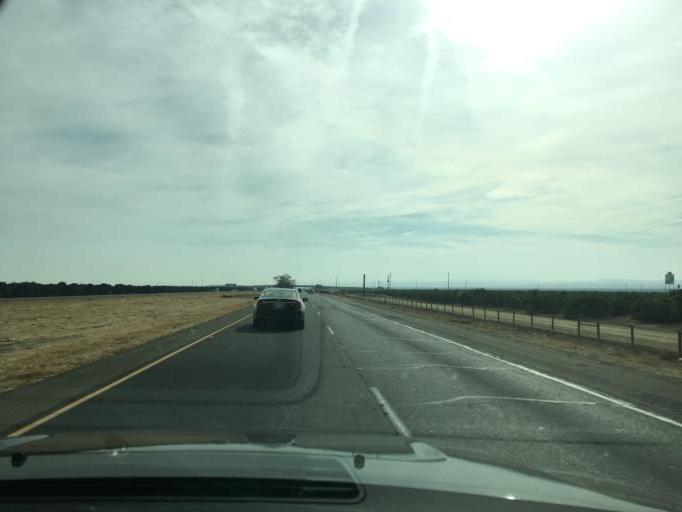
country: US
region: California
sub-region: Fresno County
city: Huron
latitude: 36.1447
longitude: -120.1655
